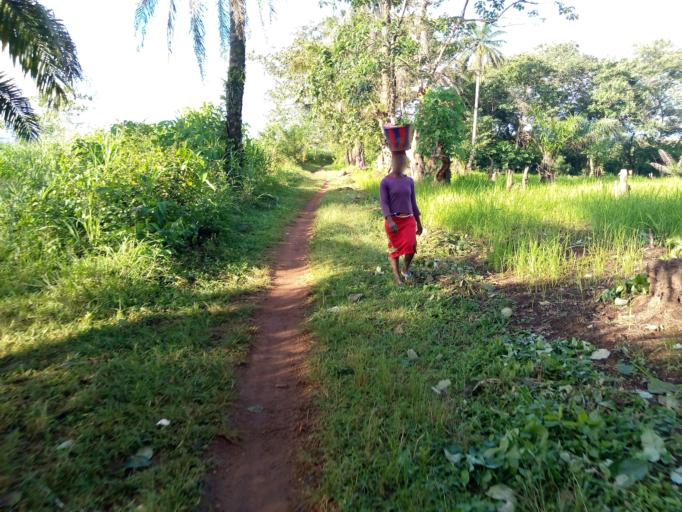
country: SL
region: Eastern Province
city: Buedu
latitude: 8.4825
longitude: -10.3261
